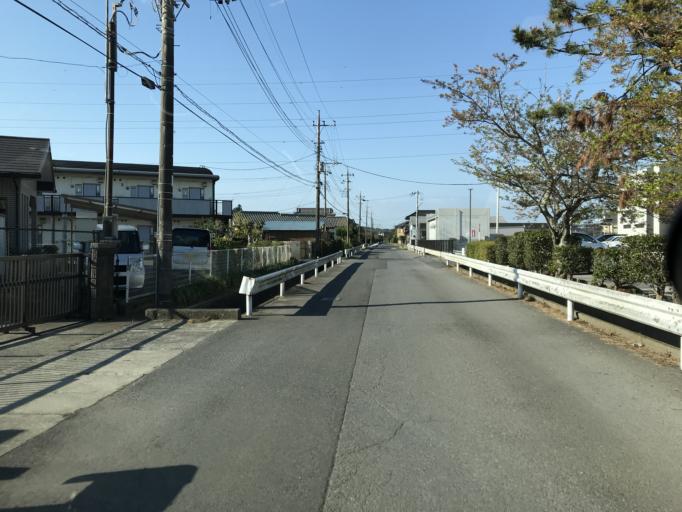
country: JP
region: Chiba
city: Omigawa
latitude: 35.8432
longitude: 140.6021
